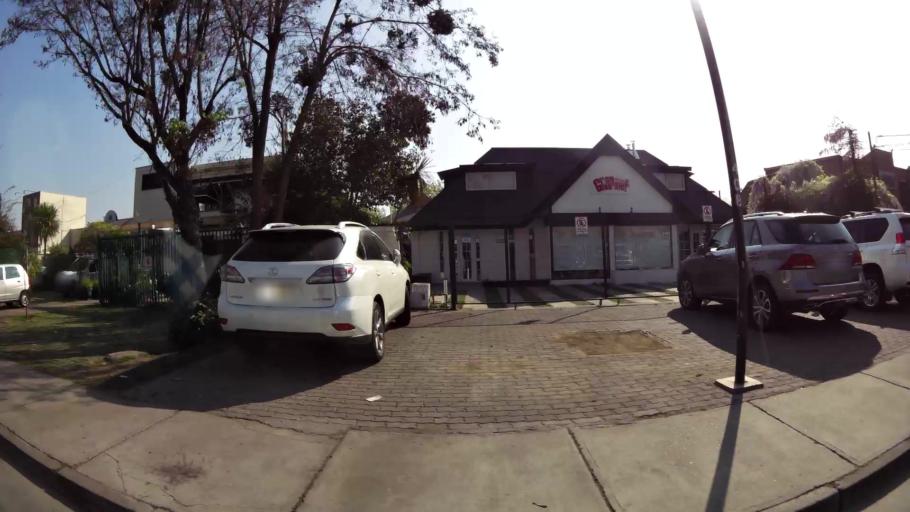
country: CL
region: Santiago Metropolitan
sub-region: Provincia de Santiago
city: Villa Presidente Frei, Nunoa, Santiago, Chile
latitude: -33.3863
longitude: -70.5530
